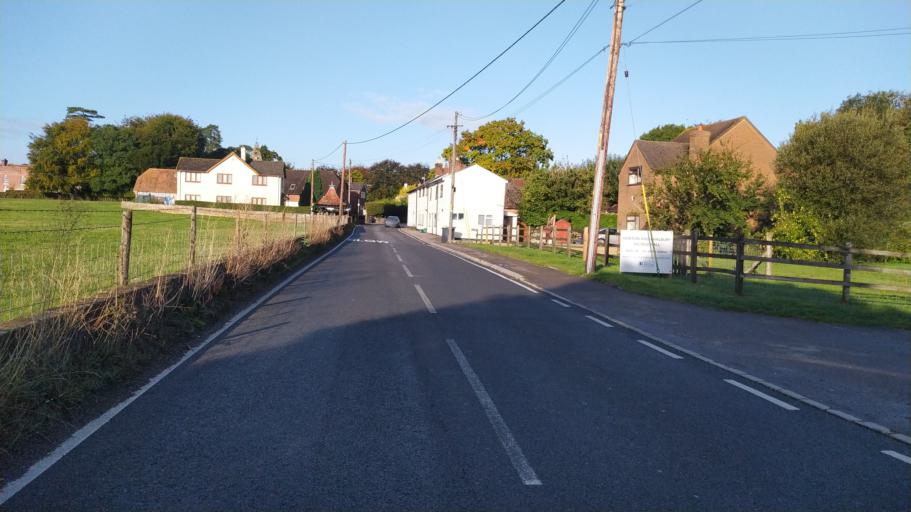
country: GB
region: England
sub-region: Dorset
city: Three Legged Cross
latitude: 50.8667
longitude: -1.9556
